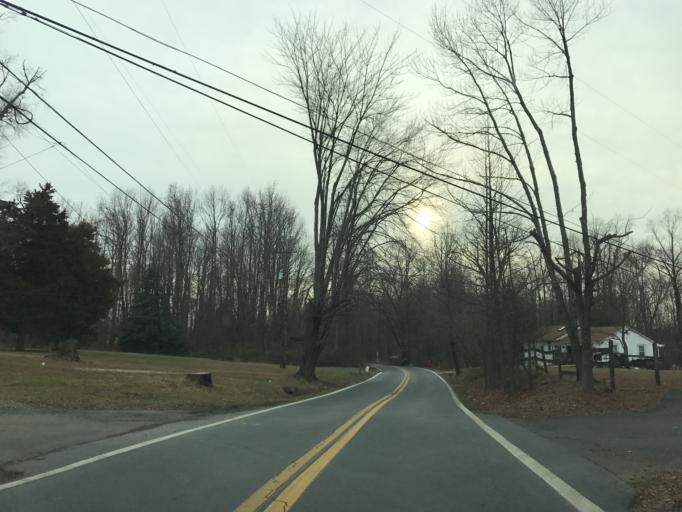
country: US
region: Maryland
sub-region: Baltimore County
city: White Marsh
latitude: 39.3941
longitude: -76.4144
